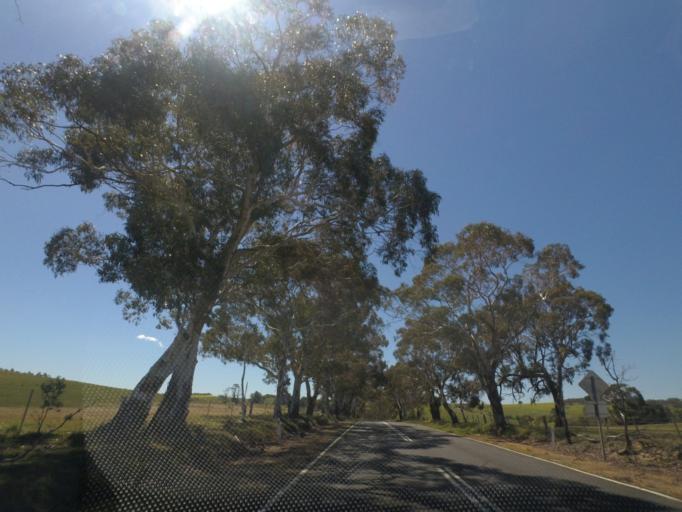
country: AU
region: Victoria
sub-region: Hume
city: Sunbury
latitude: -37.1508
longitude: 144.7712
